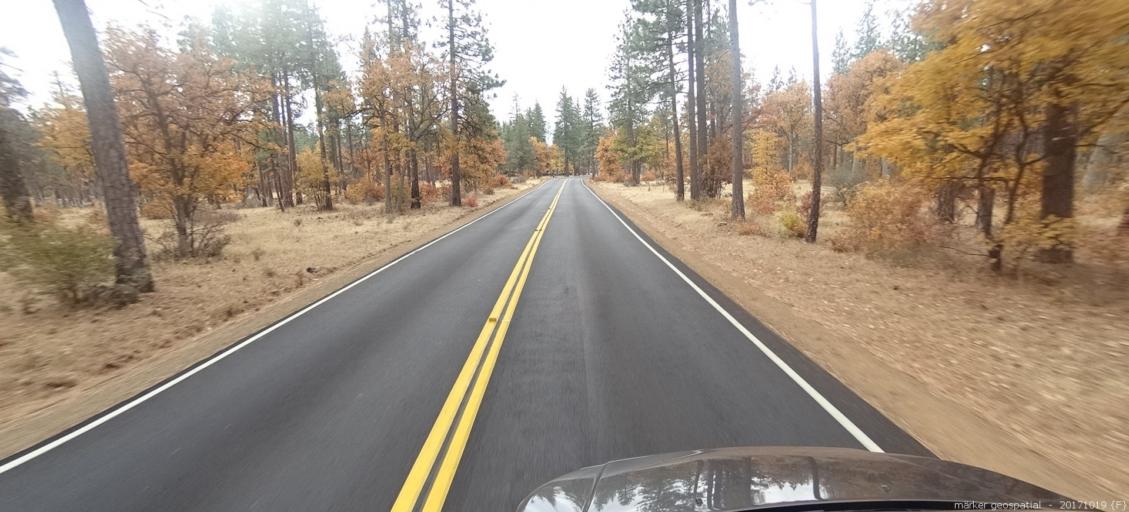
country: US
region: California
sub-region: Shasta County
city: Burney
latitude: 41.1217
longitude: -121.3323
